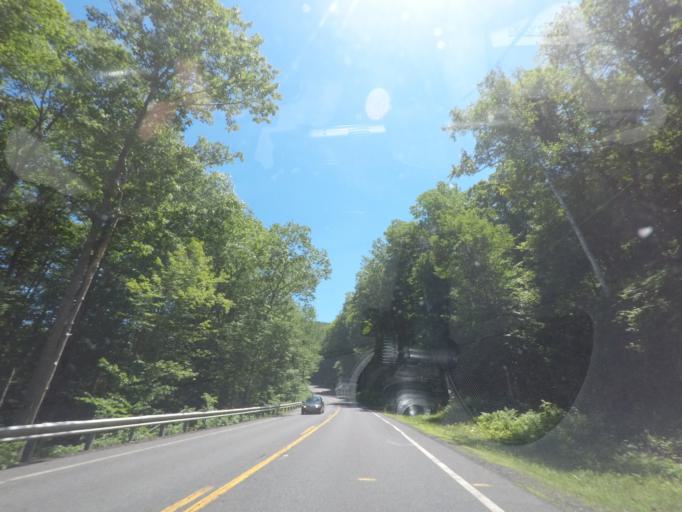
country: US
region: Massachusetts
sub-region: Hampshire County
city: Westhampton
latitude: 42.2520
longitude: -72.9321
